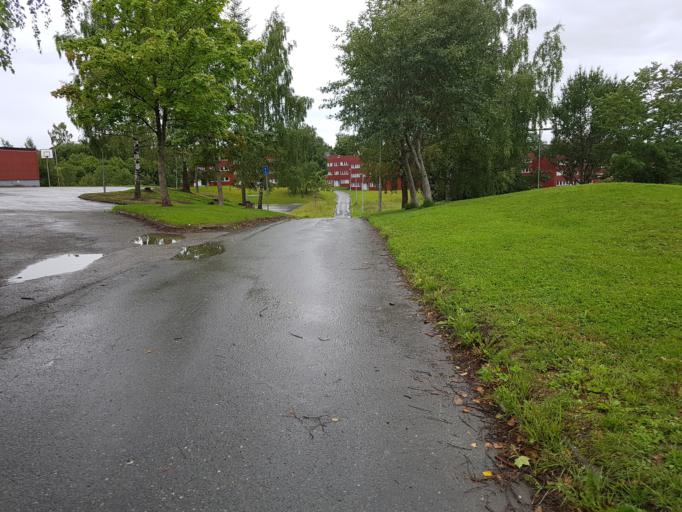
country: NO
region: Sor-Trondelag
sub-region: Trondheim
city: Trondheim
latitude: 63.4008
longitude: 10.4323
